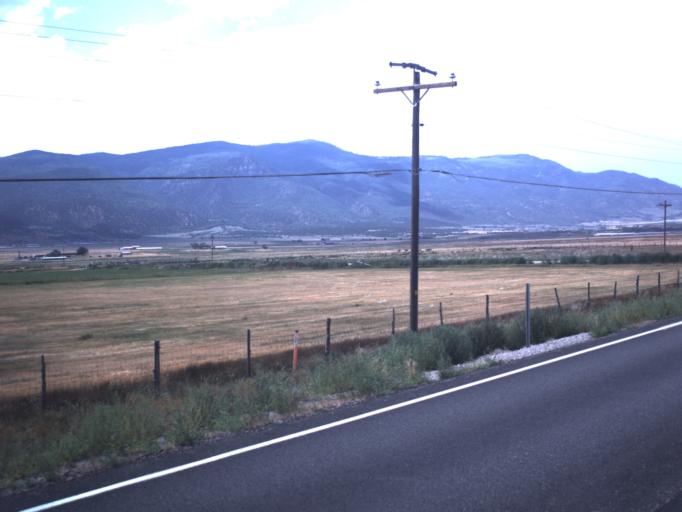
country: US
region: Utah
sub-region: Sanpete County
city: Moroni
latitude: 39.5668
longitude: -111.6052
